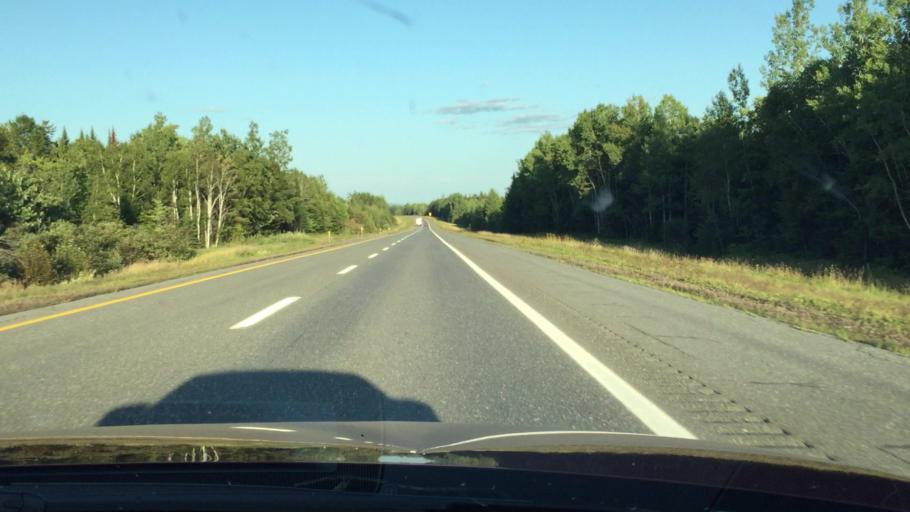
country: US
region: Maine
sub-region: Aroostook County
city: Hodgdon
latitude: 46.1420
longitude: -68.0343
